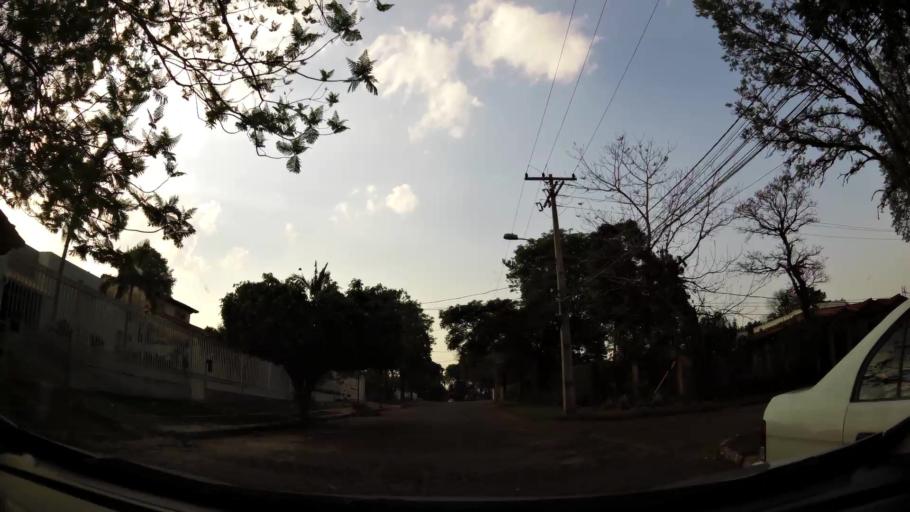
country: PY
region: Alto Parana
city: Presidente Franco
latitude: -25.5189
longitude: -54.6395
